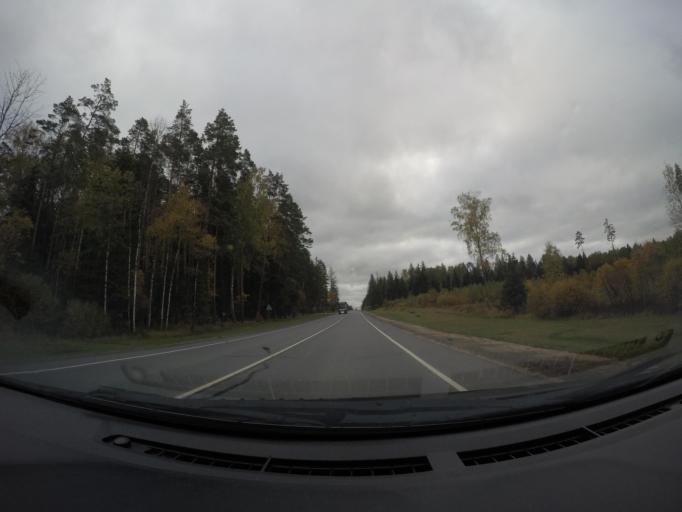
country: RU
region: Moskovskaya
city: Dorokhovo
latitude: 55.6143
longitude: 36.3489
